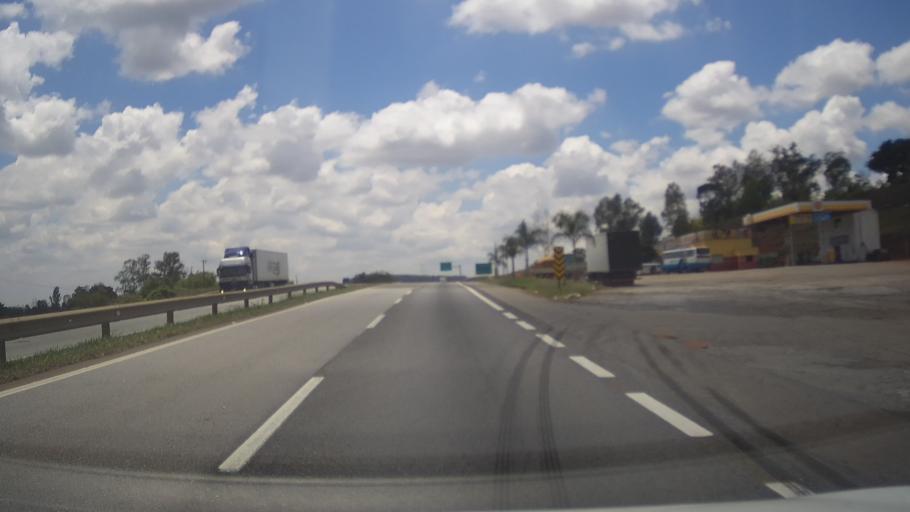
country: BR
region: Minas Gerais
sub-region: Campanha
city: Campanha
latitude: -21.7895
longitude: -45.4433
